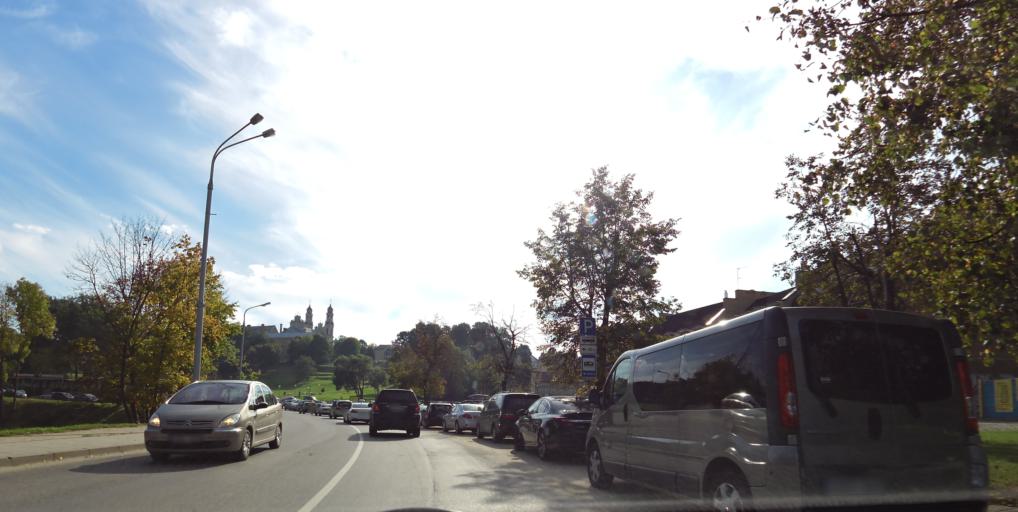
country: LT
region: Vilnius County
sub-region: Vilnius
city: Vilnius
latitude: 54.6794
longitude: 25.2929
